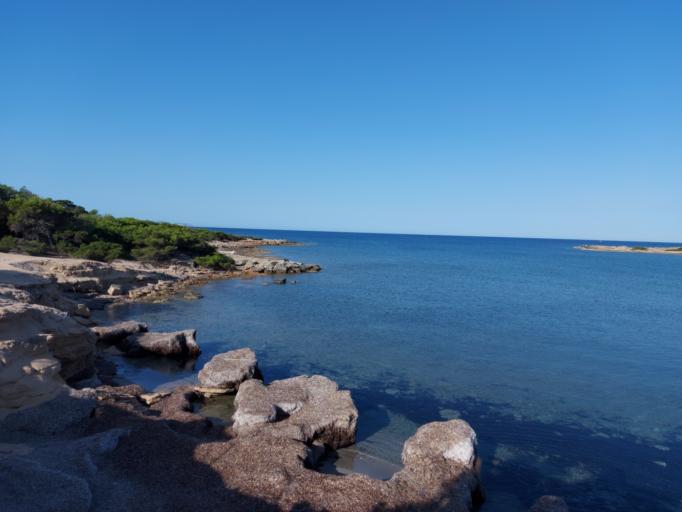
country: ES
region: Balearic Islands
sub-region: Illes Balears
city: Ses Salines
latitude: 39.2887
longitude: 3.0312
